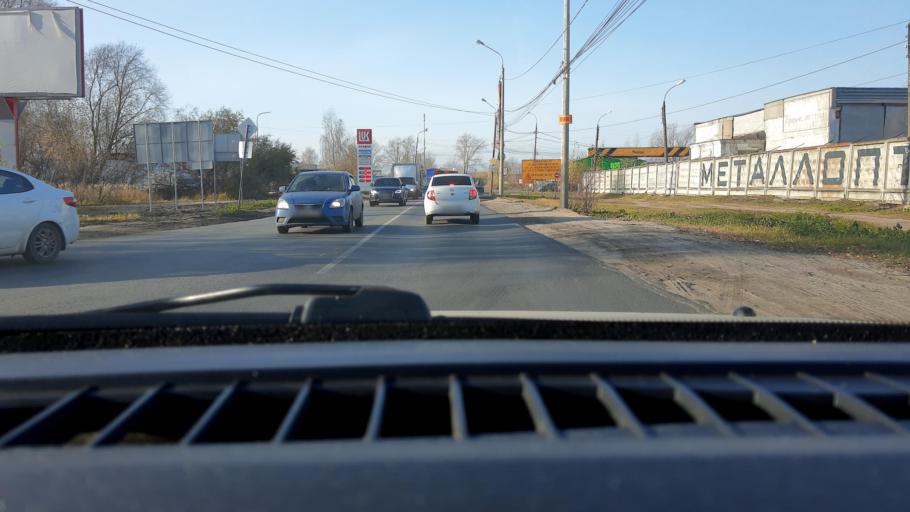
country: RU
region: Nizjnij Novgorod
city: Gorbatovka
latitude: 56.3512
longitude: 43.8038
